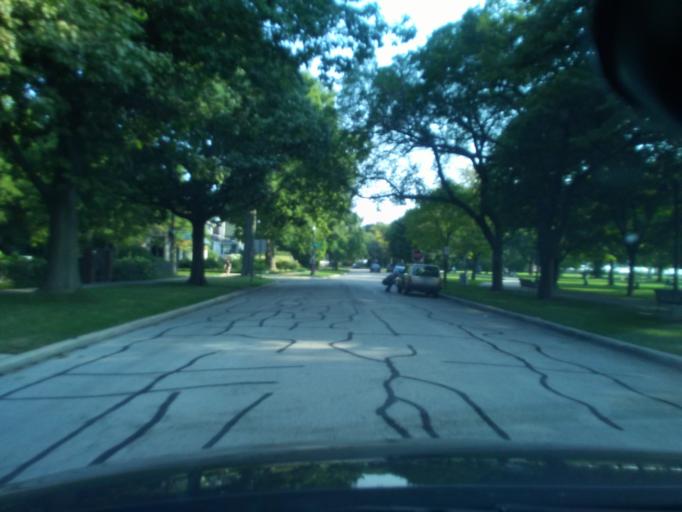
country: US
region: Illinois
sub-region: Cook County
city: Evanston
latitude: 42.0387
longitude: -87.6705
